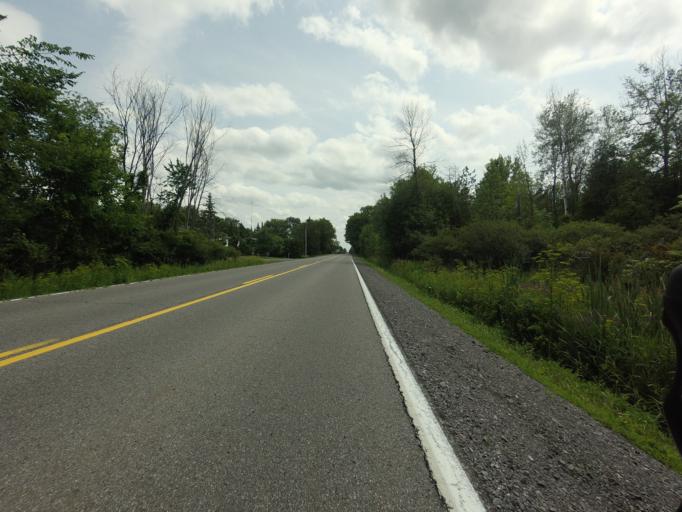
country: CA
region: Ontario
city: Ottawa
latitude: 45.2150
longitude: -75.5998
